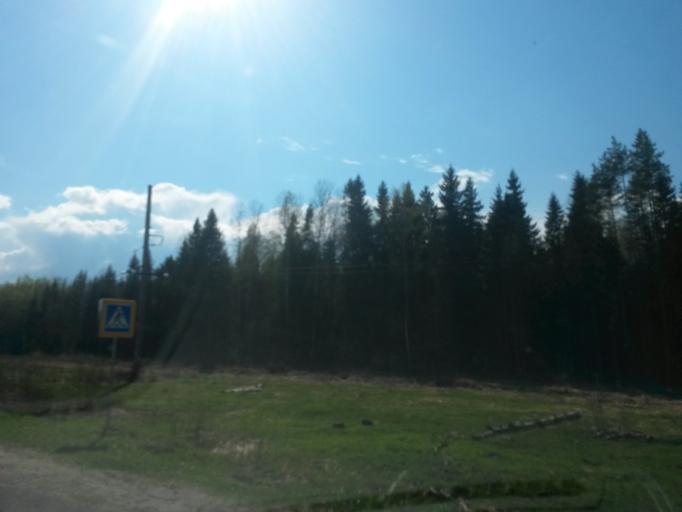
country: RU
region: Jaroslavl
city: Tutayev
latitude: 57.9716
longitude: 39.5084
